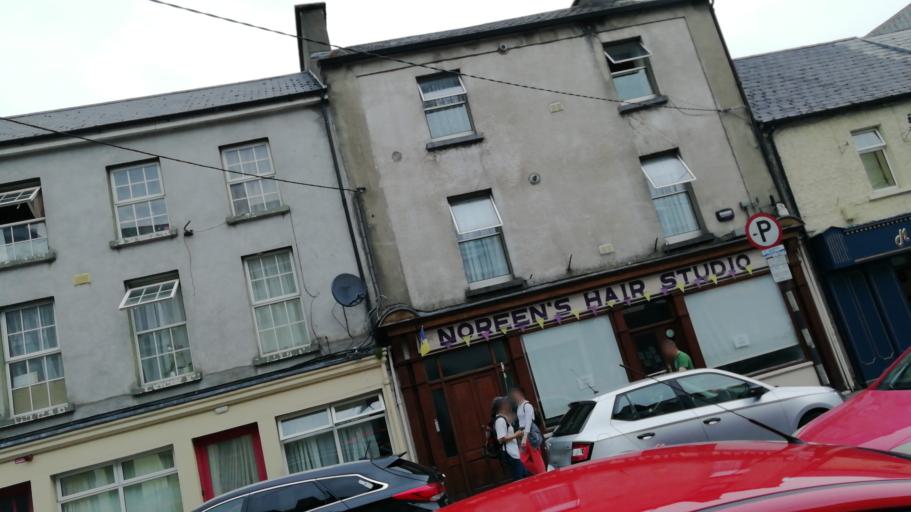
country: IE
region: Munster
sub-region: South Tipperary
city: Cluain Meala
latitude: 52.3521
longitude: -7.7076
